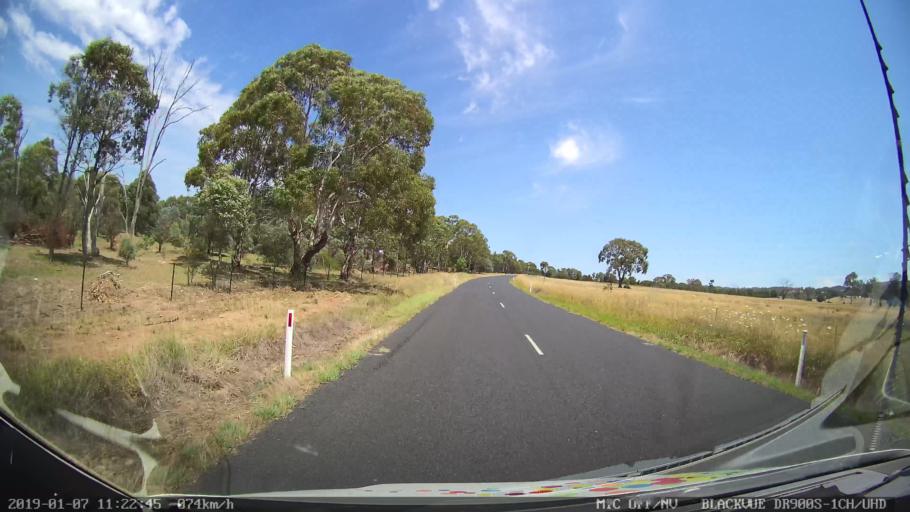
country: AU
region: New South Wales
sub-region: Armidale Dumaresq
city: Armidale
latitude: -30.4806
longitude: 151.6280
